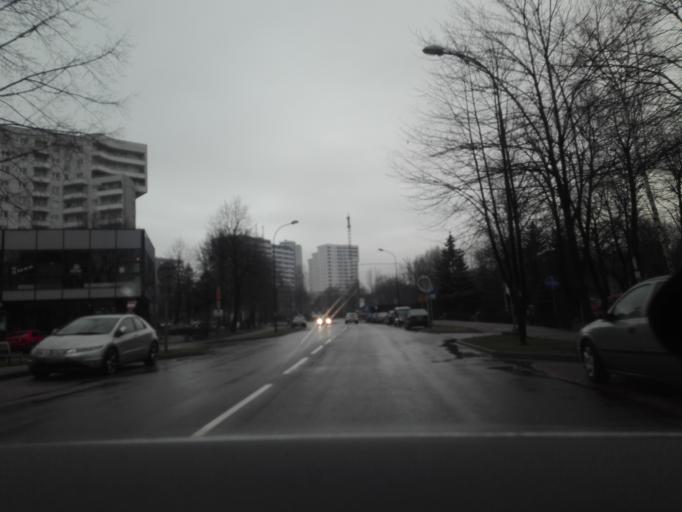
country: PL
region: Silesian Voivodeship
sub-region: Chorzow
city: Chorzow
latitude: 50.2747
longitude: 18.9854
